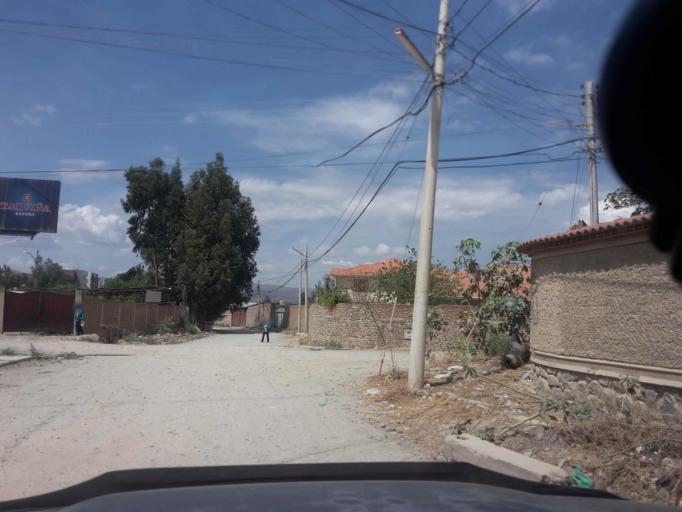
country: BO
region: Cochabamba
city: Cochabamba
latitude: -17.3481
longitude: -66.2029
